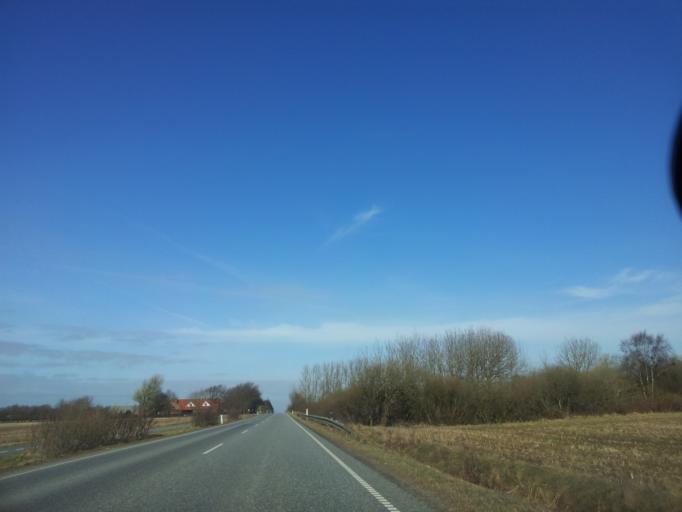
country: DK
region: South Denmark
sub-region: Esbjerg Kommune
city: Ribe
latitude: 55.2917
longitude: 8.7386
